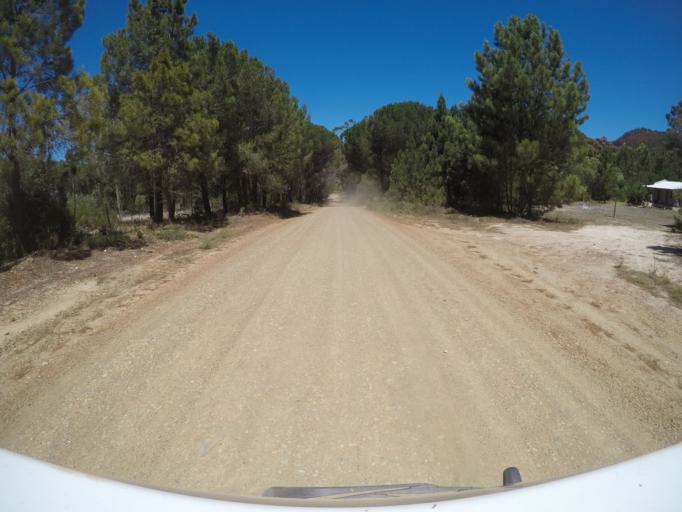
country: ZA
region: Western Cape
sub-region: Overberg District Municipality
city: Grabouw
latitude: -34.1627
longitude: 19.2247
